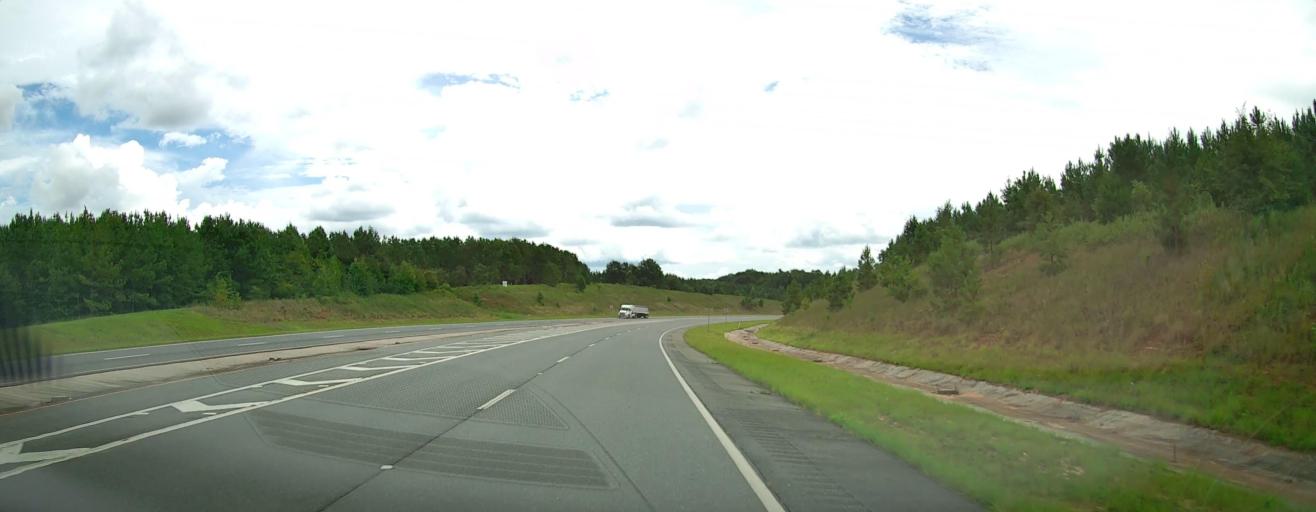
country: US
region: Georgia
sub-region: Schley County
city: Ellaville
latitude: 32.2529
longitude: -84.2997
